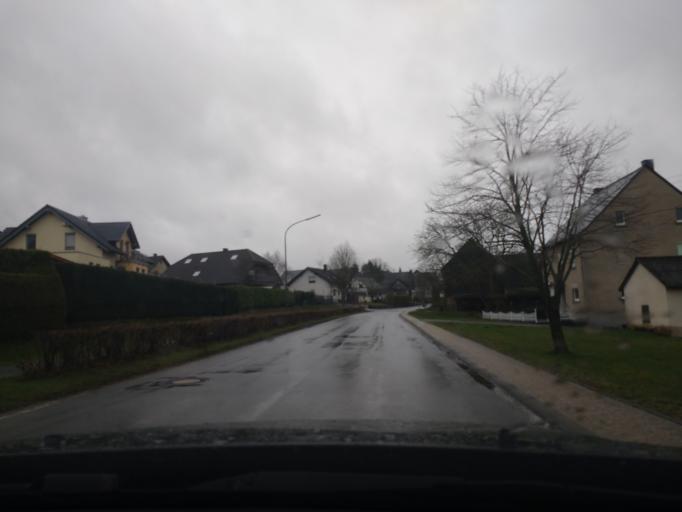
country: DE
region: Rheinland-Pfalz
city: Irmenach
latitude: 49.9185
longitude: 7.1872
